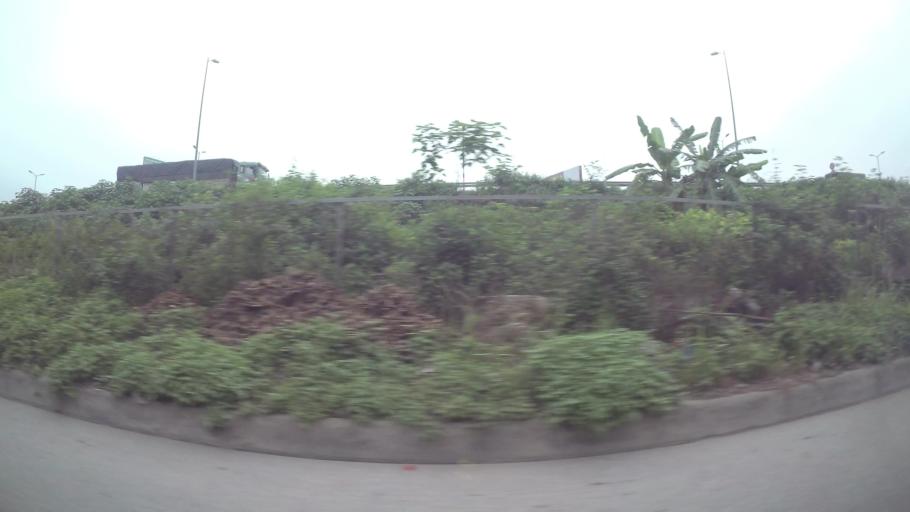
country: VN
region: Ha Noi
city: Hai BaTrung
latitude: 20.9816
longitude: 105.8904
